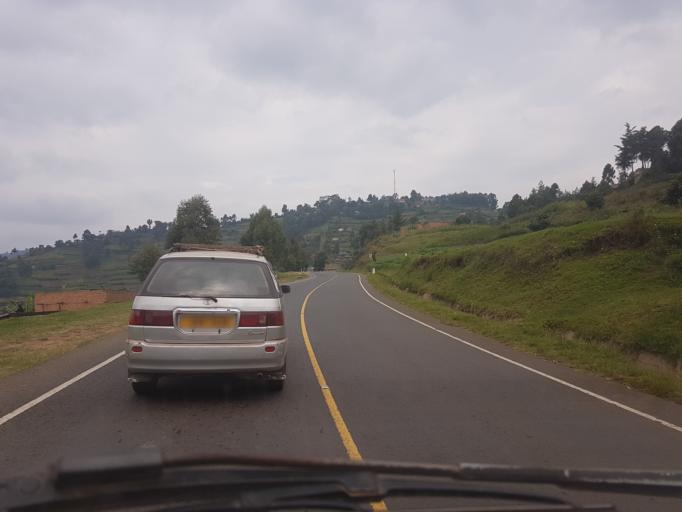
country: UG
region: Western Region
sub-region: Kisoro District
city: Kisoro
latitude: -1.2022
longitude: 29.8127
